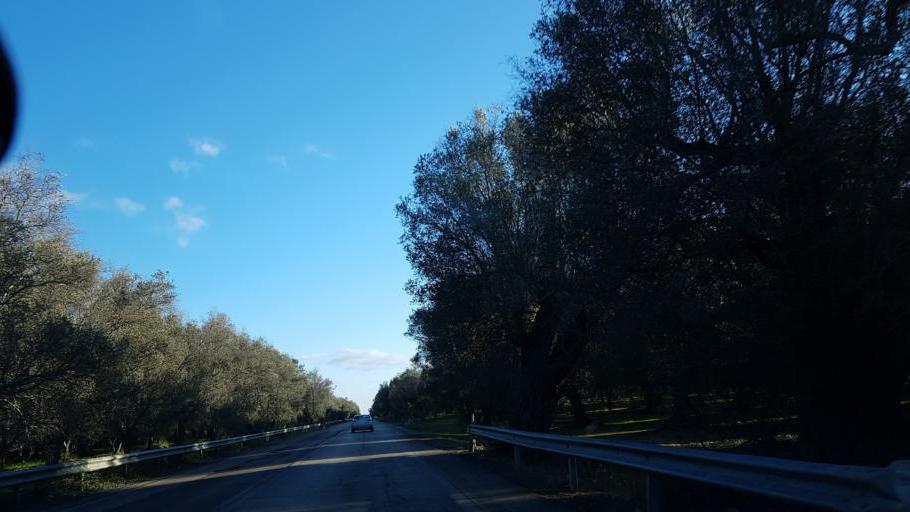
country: IT
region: Apulia
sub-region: Provincia di Brindisi
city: San Pietro Vernotico
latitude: 40.4681
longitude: 18.0148
